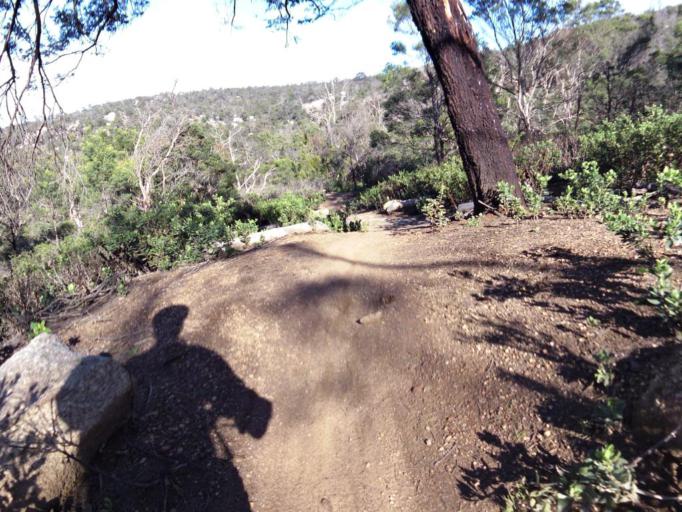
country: AU
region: Victoria
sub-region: Wyndham
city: Little River
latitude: -37.9258
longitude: 144.4353
